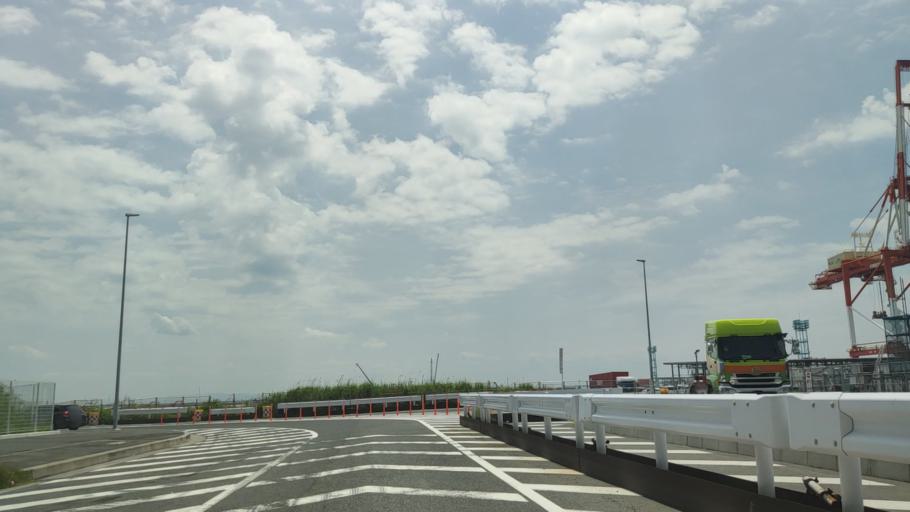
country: JP
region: Kanagawa
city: Yokohama
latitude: 35.4051
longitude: 139.6846
